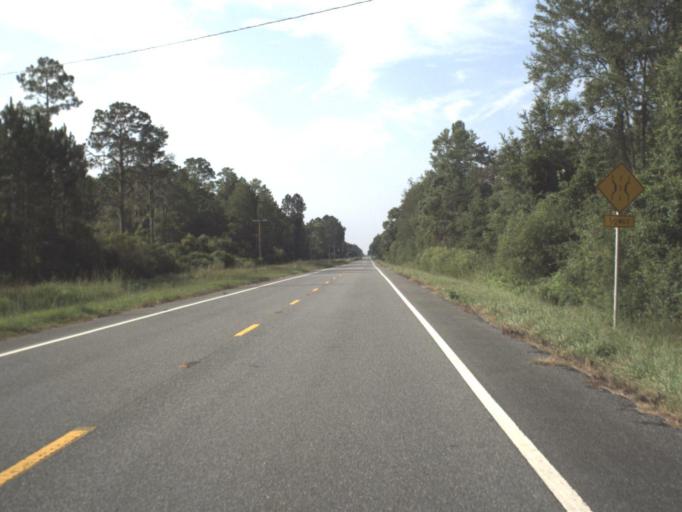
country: US
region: Florida
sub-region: Taylor County
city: Perry
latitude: 30.2604
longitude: -83.6252
